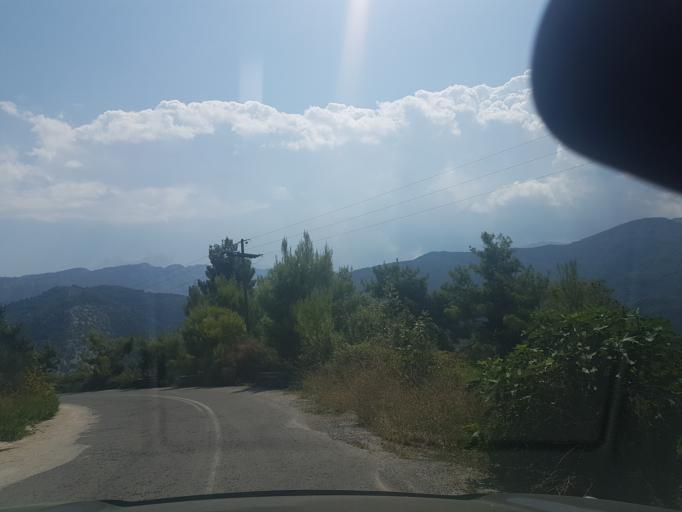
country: GR
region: Central Greece
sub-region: Nomos Evvoias
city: Kymi
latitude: 38.6563
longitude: 23.9157
